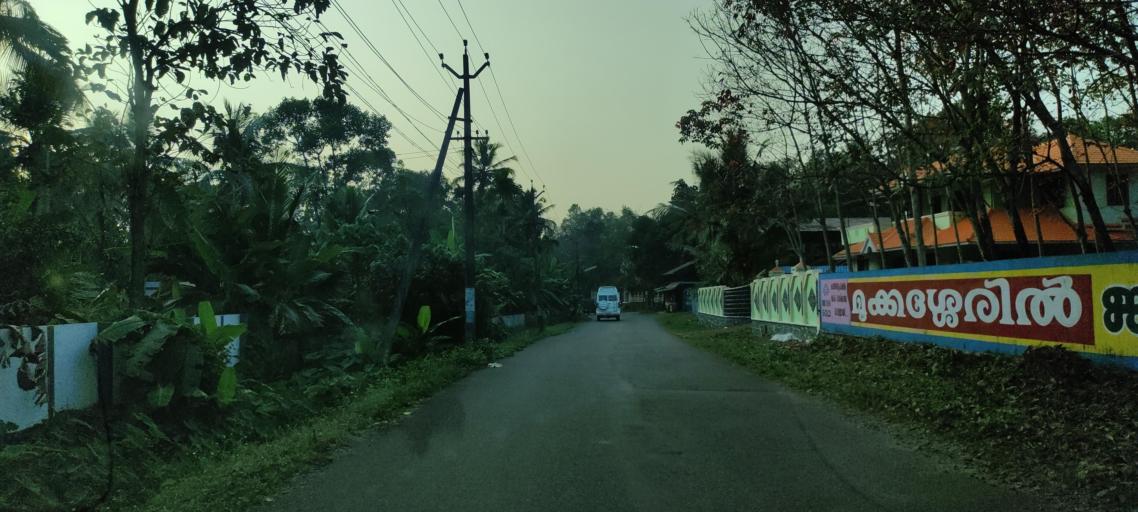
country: IN
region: Kerala
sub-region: Alappuzha
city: Kattanam
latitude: 9.1441
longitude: 76.5701
